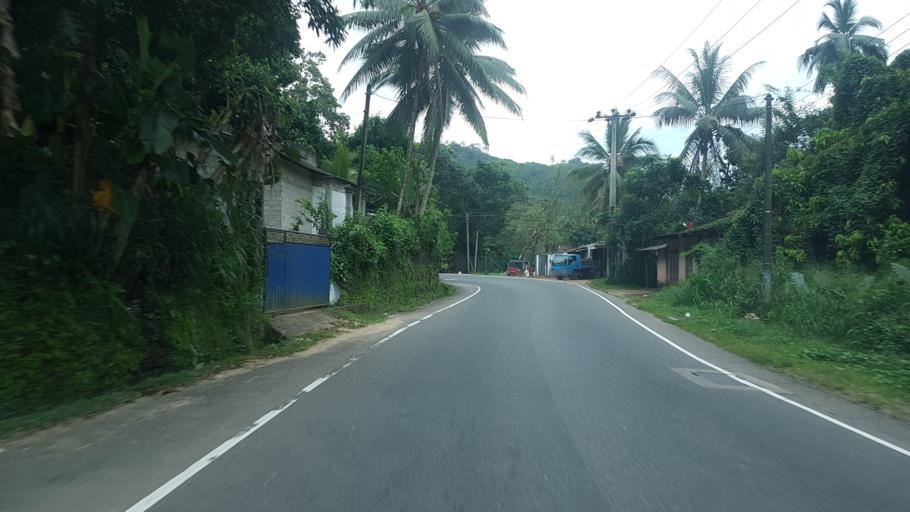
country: LK
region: Western
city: Hanwella Ihala
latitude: 7.0233
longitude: 80.2666
